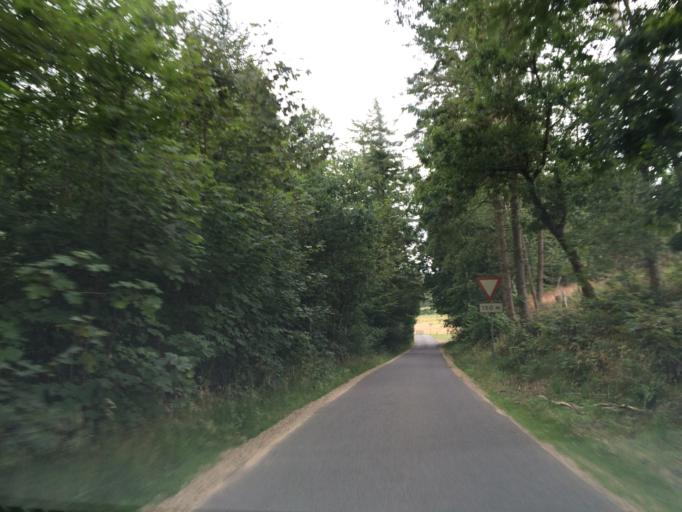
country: DK
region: Central Jutland
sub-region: Silkeborg Kommune
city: Svejbaek
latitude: 56.2046
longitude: 9.6461
